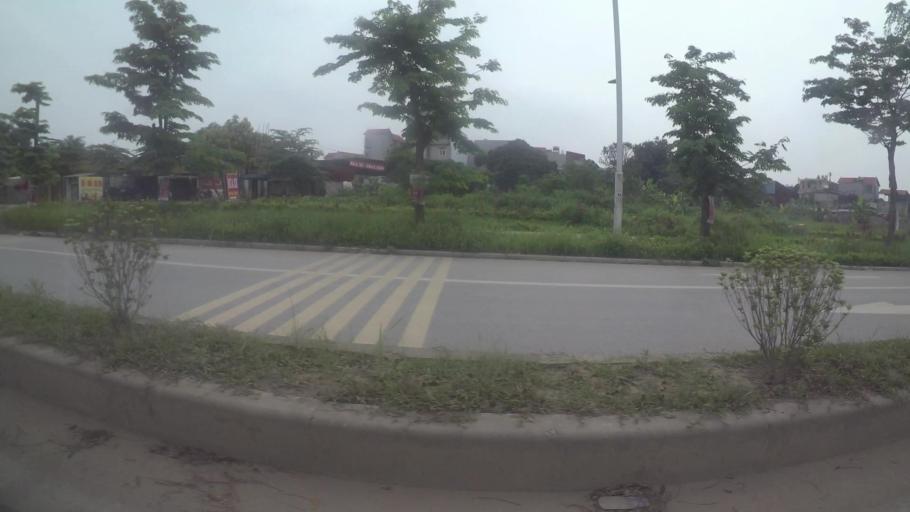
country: VN
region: Ha Noi
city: Cau Dien
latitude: 21.0399
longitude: 105.7409
